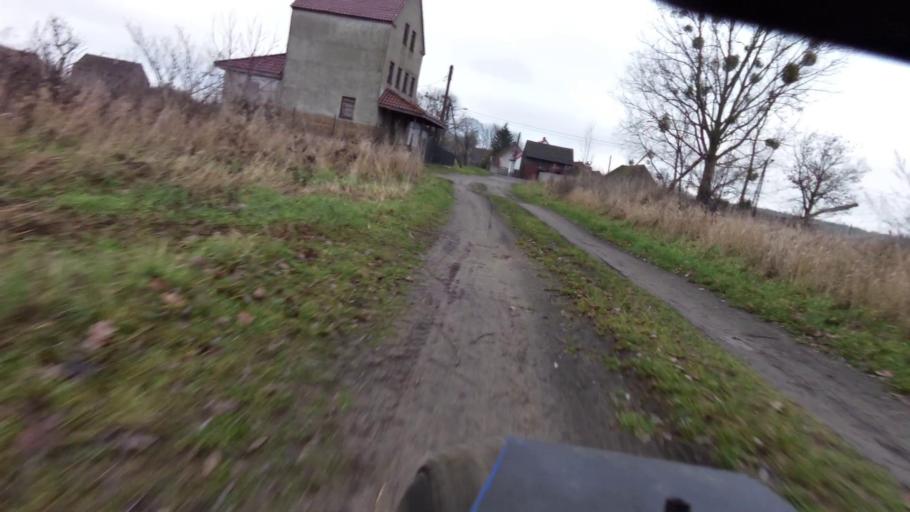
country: PL
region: Lubusz
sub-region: Powiat gorzowski
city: Witnica
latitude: 52.6748
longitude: 14.7948
